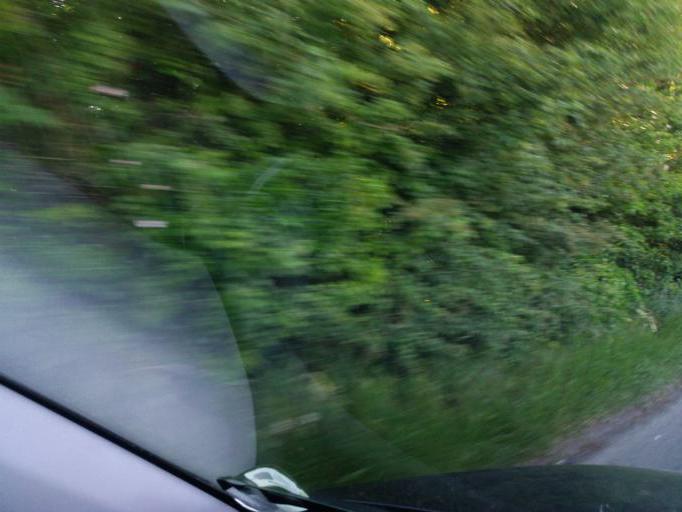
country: IE
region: Leinster
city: Ballymun
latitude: 53.4498
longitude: -6.2941
